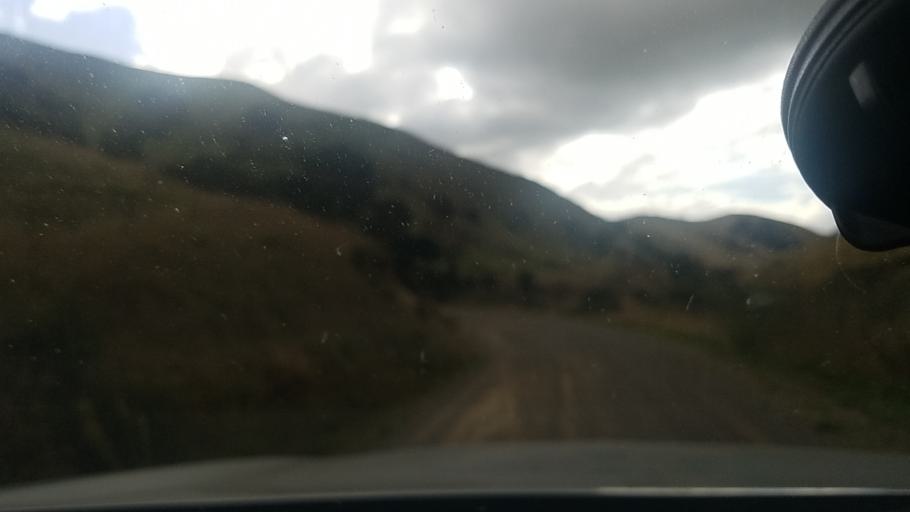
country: NZ
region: Marlborough
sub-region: Marlborough District
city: Blenheim
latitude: -41.5851
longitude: 174.0669
